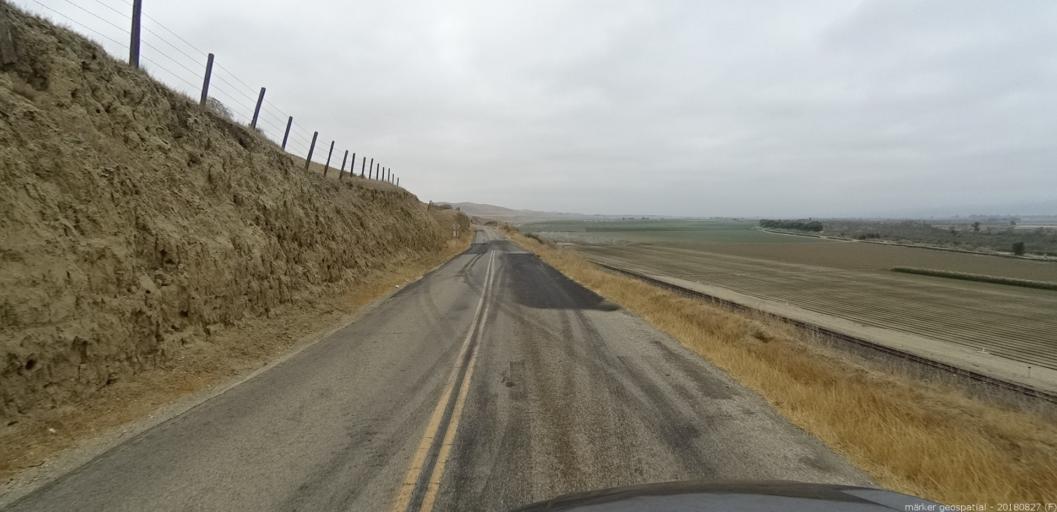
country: US
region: California
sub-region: Monterey County
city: Greenfield
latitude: 36.3193
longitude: -121.1782
